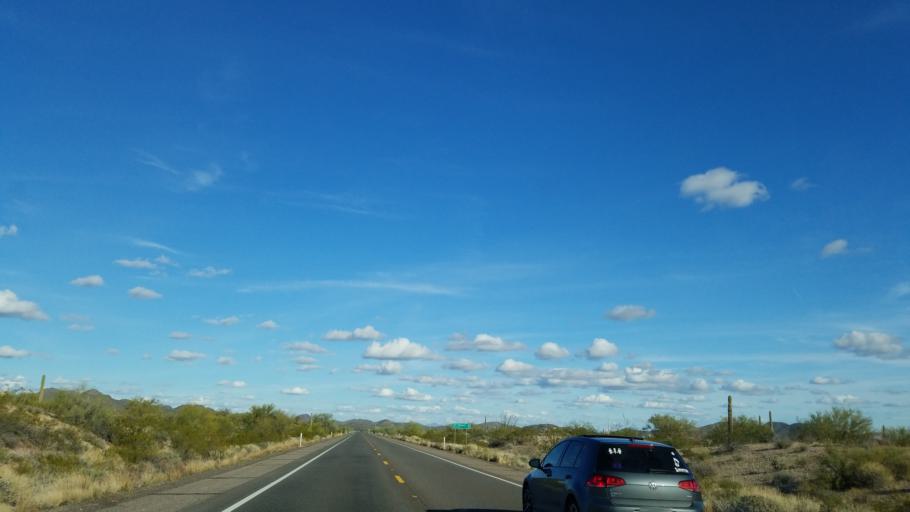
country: US
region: Arizona
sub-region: Maricopa County
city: Sun City West
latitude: 33.8320
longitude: -112.4425
